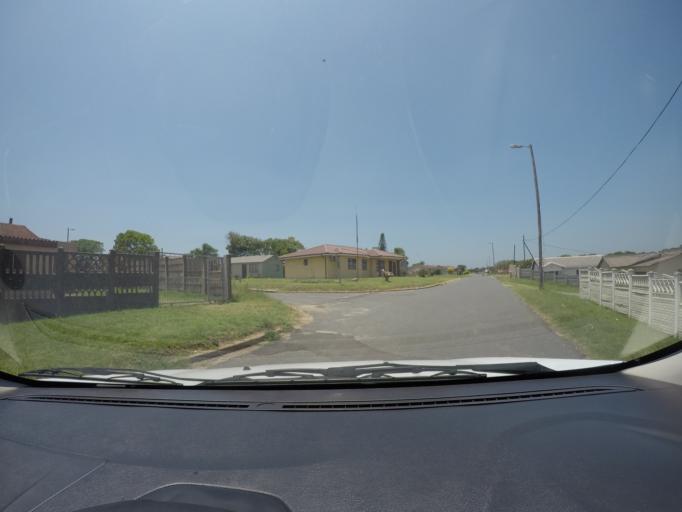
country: ZA
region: KwaZulu-Natal
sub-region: uThungulu District Municipality
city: eSikhawini
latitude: -28.8749
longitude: 31.9068
